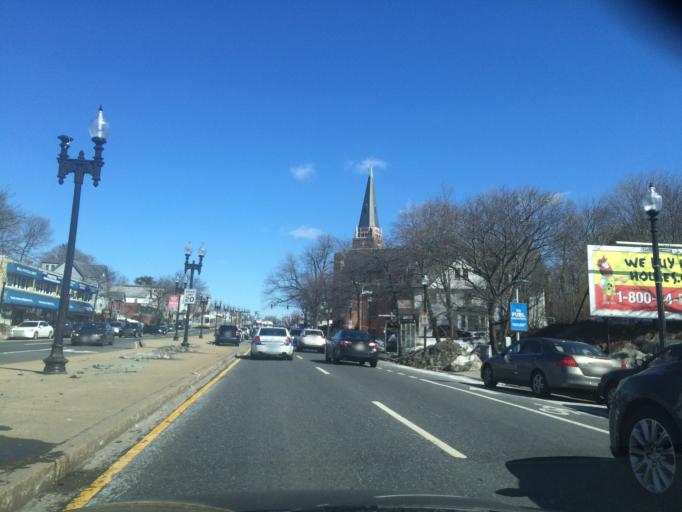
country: US
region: Massachusetts
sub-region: Norfolk County
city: Milton
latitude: 42.2702
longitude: -71.0936
